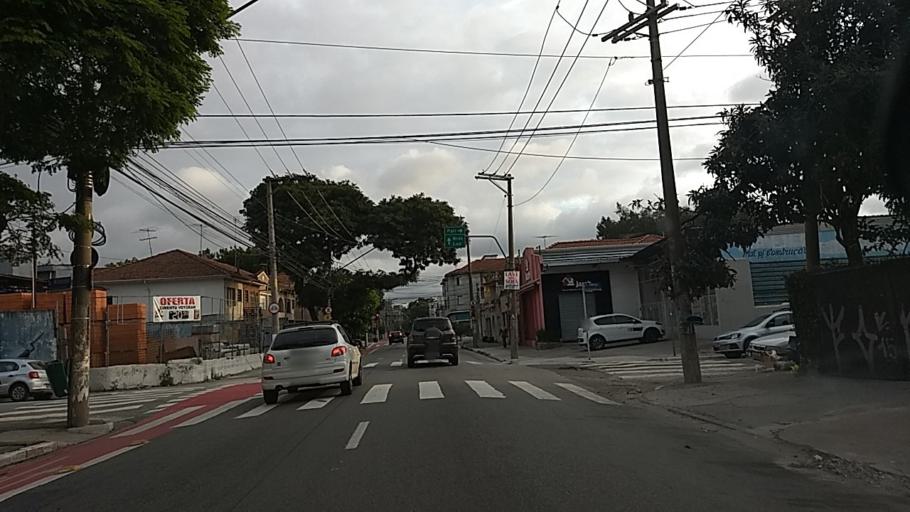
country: BR
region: Sao Paulo
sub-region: Sao Paulo
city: Sao Paulo
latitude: -23.5279
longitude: -46.6084
